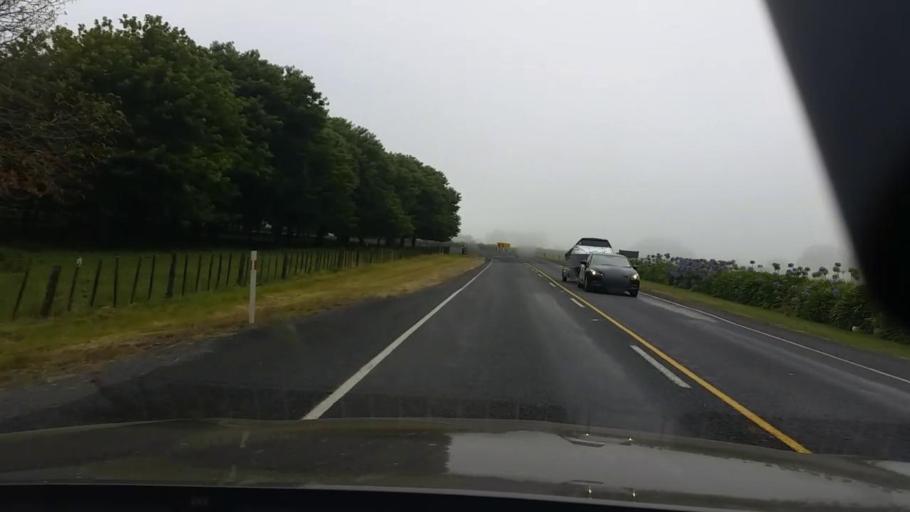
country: NZ
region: Waikato
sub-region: Hamilton City
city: Hamilton
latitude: -37.6527
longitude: 175.2965
